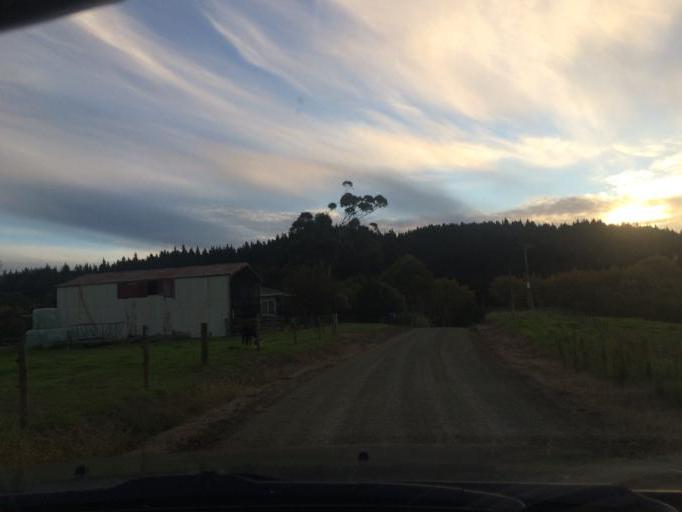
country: NZ
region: Northland
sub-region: Whangarei
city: Maungatapere
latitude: -35.8106
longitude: 174.0392
